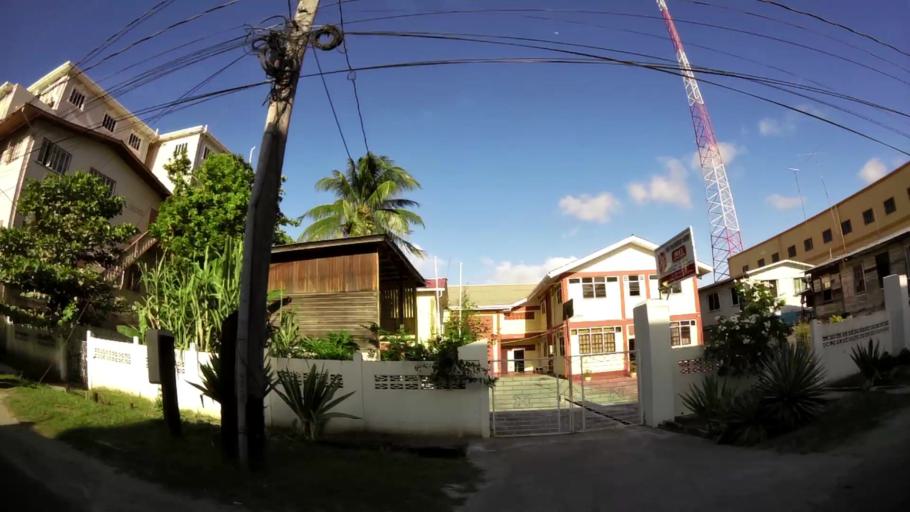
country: GY
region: Demerara-Mahaica
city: Georgetown
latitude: 6.8223
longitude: -58.1650
